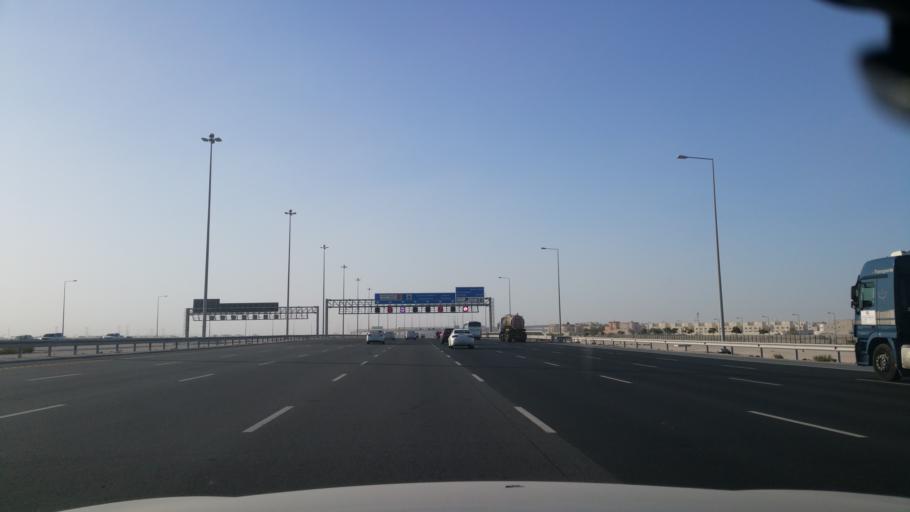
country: QA
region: Al Wakrah
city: Al Wukayr
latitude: 25.1723
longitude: 51.5575
